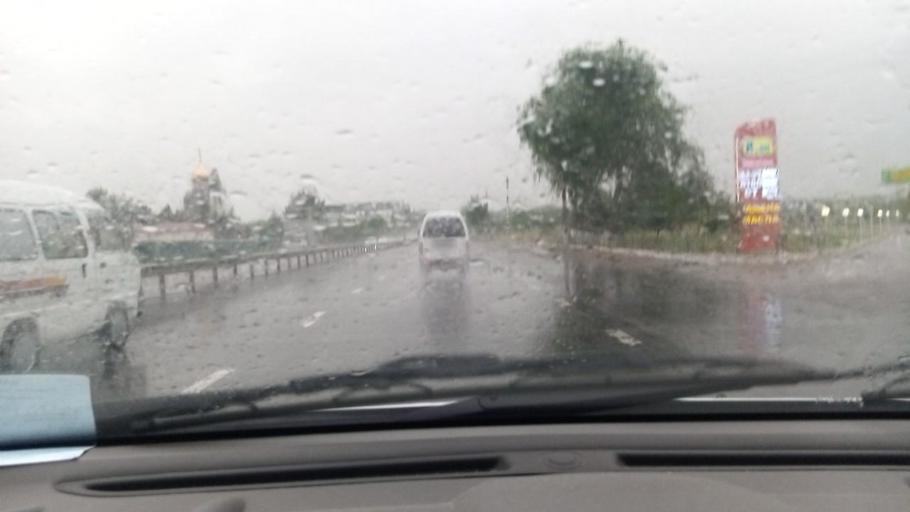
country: UZ
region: Toshkent
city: Tuytepa
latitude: 41.1216
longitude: 69.4409
